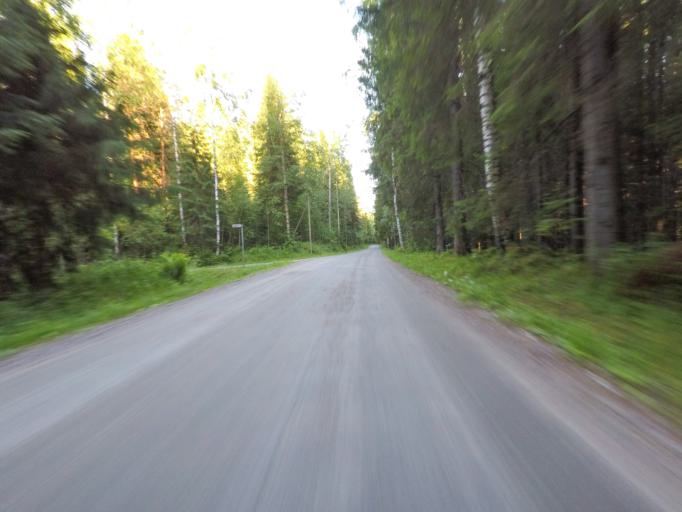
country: FI
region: Northern Savo
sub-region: Kuopio
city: Maaninka
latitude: 62.8833
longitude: 27.2904
